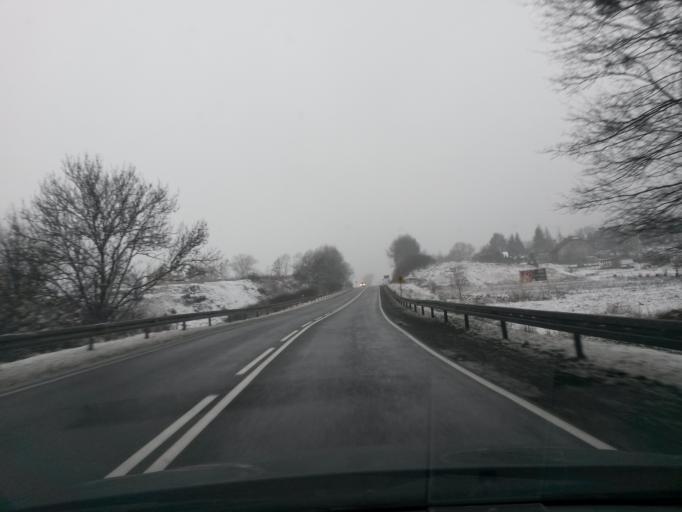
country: PL
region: Kujawsko-Pomorskie
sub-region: Powiat bydgoski
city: Biale Blota
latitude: 53.1563
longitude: 17.8659
